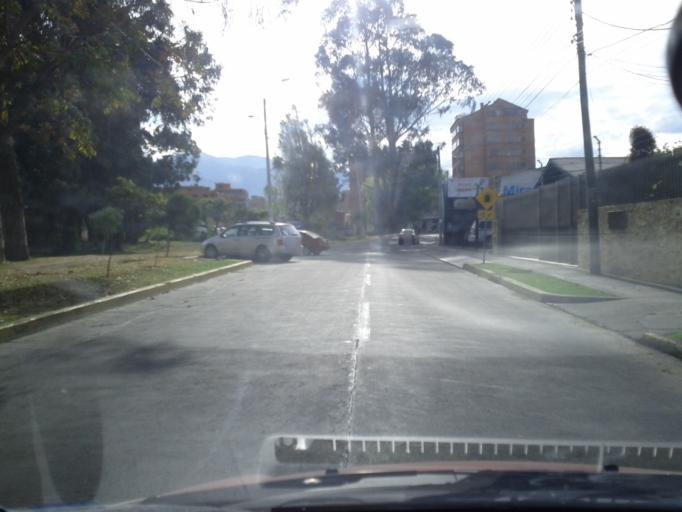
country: EC
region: Azuay
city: Cuenca
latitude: -2.8926
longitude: -79.0199
